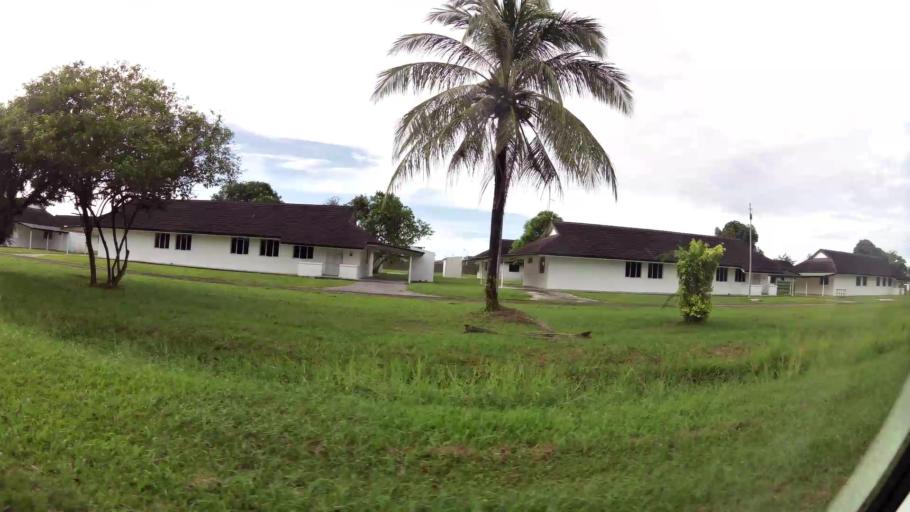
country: BN
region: Belait
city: Seria
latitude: 4.6104
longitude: 114.3261
